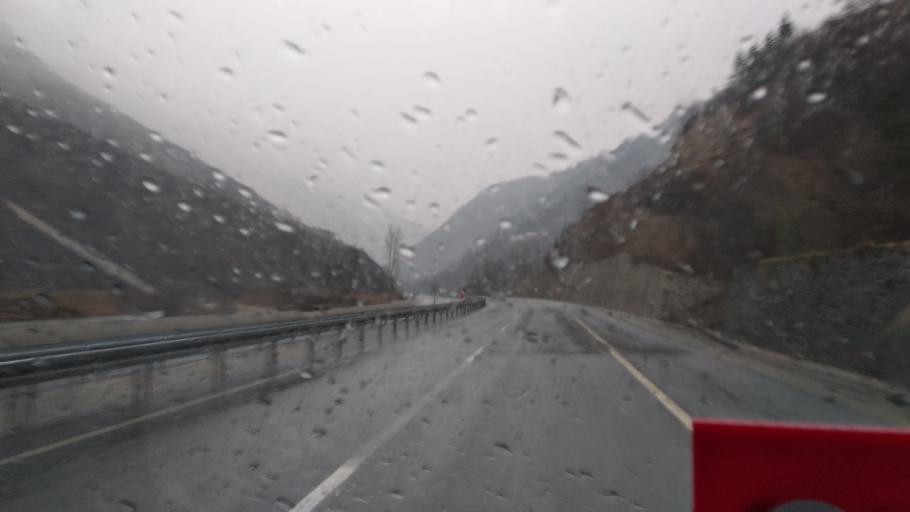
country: TR
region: Trabzon
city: Macka
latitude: 40.7847
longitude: 39.5758
